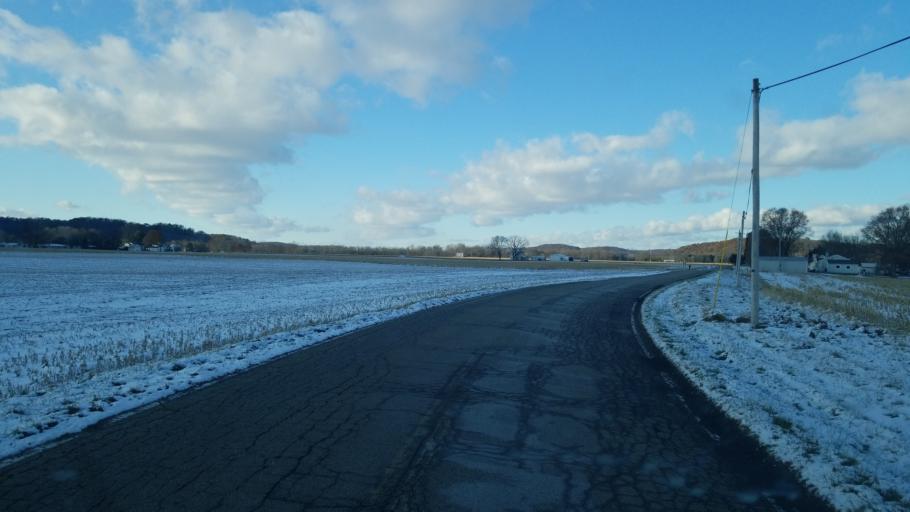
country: US
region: Ohio
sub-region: Licking County
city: Utica
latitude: 40.1679
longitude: -82.4078
